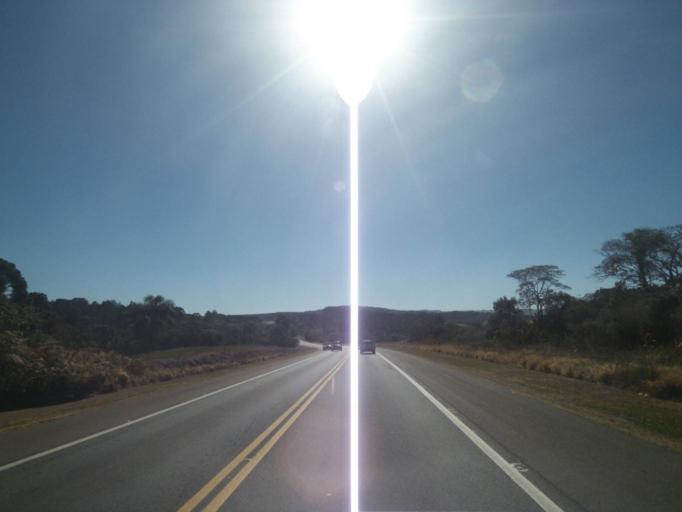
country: BR
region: Parana
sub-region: Tibagi
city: Tibagi
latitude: -24.7257
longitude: -50.5383
